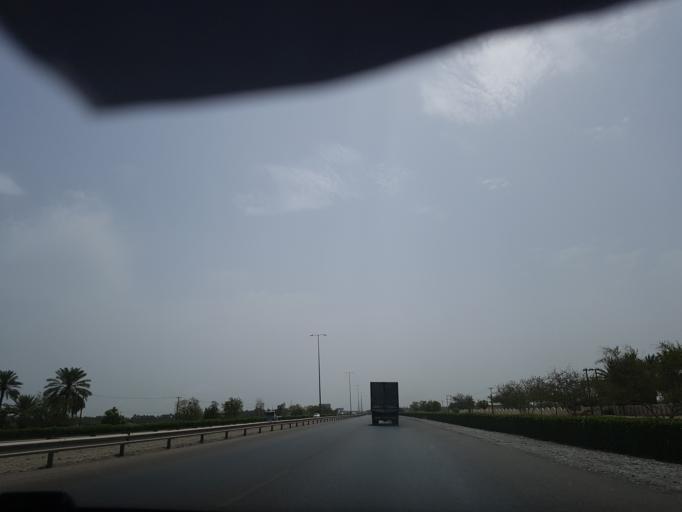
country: OM
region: Al Batinah
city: Barka'
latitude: 23.7366
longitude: 57.6608
